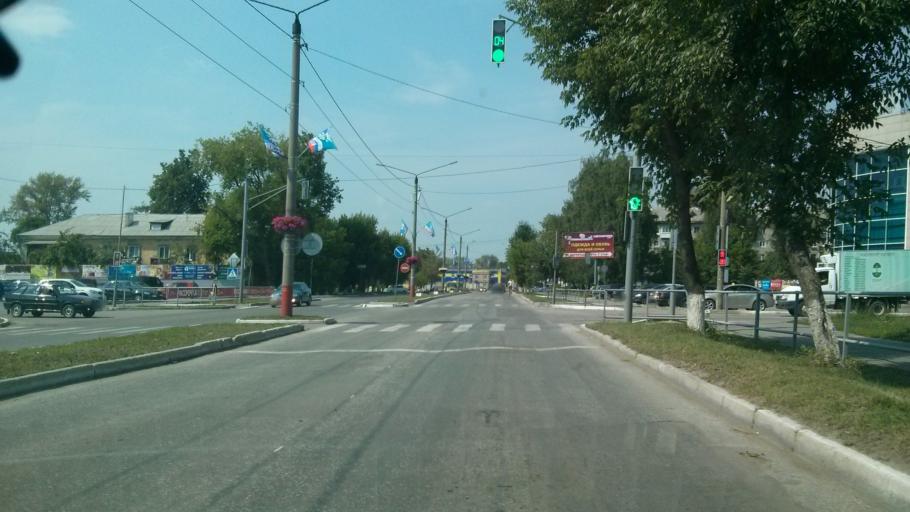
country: RU
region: Vladimir
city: Murom
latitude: 55.5699
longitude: 42.0393
